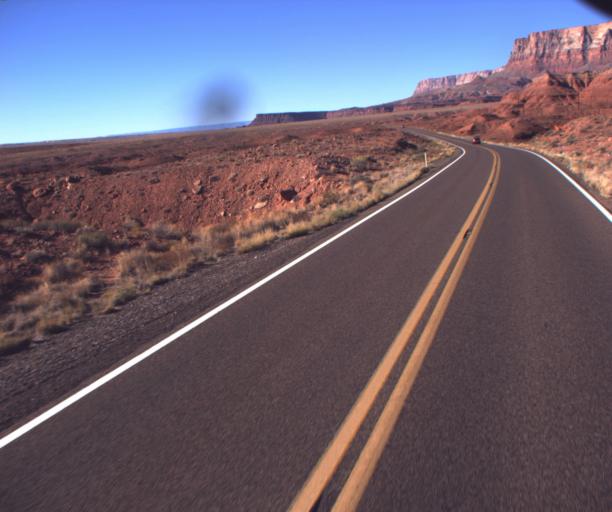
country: US
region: Arizona
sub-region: Coconino County
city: Page
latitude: 36.8074
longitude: -111.6685
